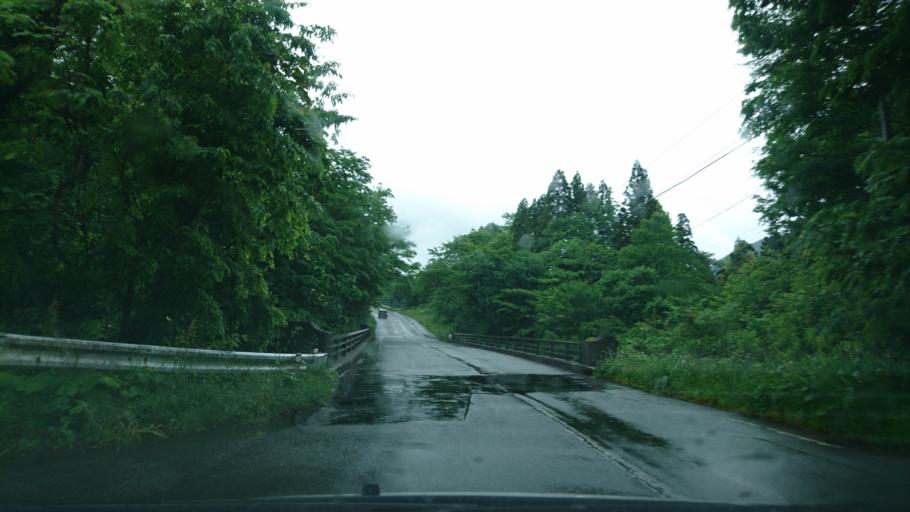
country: JP
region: Iwate
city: Ichinoseki
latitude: 38.9948
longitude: 140.9021
